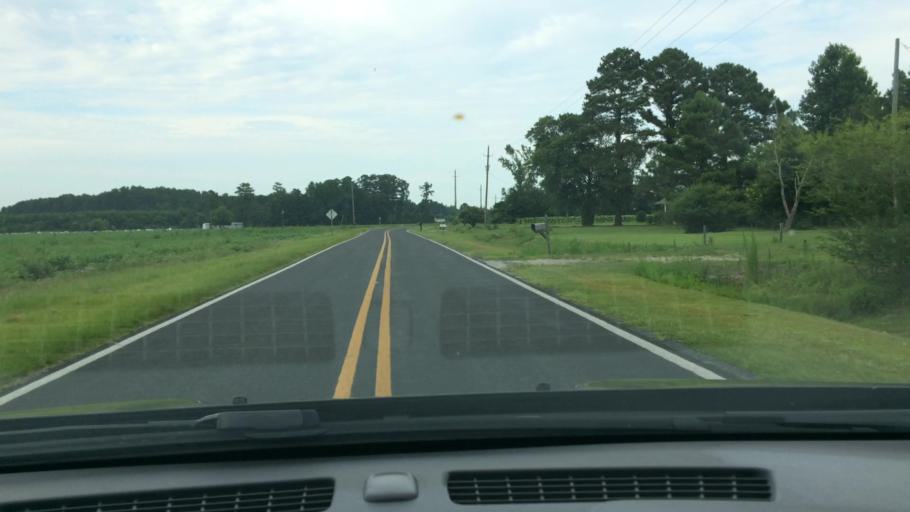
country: US
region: North Carolina
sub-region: Pitt County
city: Ayden
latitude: 35.4313
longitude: -77.4104
